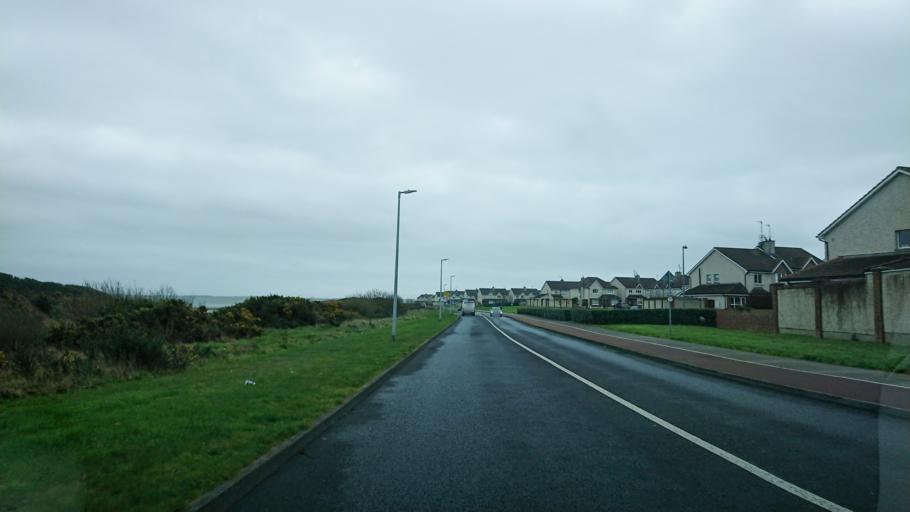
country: IE
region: Munster
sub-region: Waterford
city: Tra Mhor
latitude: 52.1717
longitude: -7.1368
